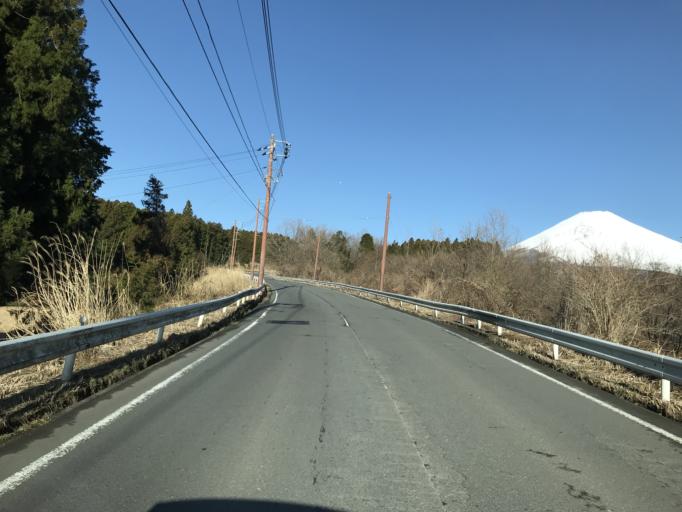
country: JP
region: Shizuoka
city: Gotemba
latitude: 35.2626
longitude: 138.8560
